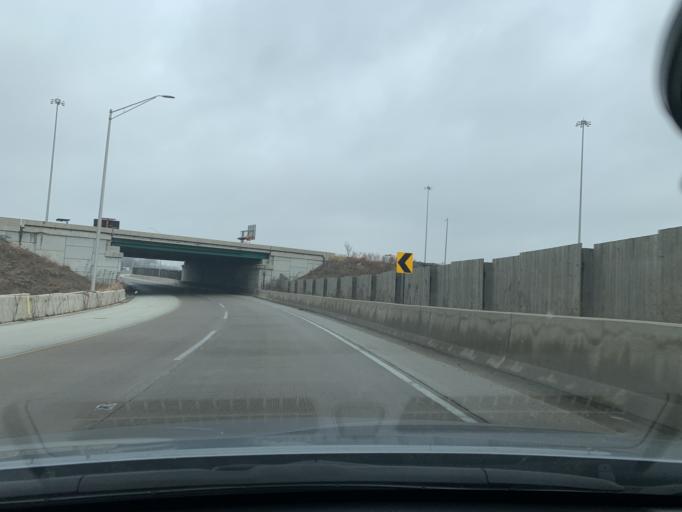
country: US
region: Illinois
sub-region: Cook County
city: Posen
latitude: 41.6180
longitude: -87.6859
